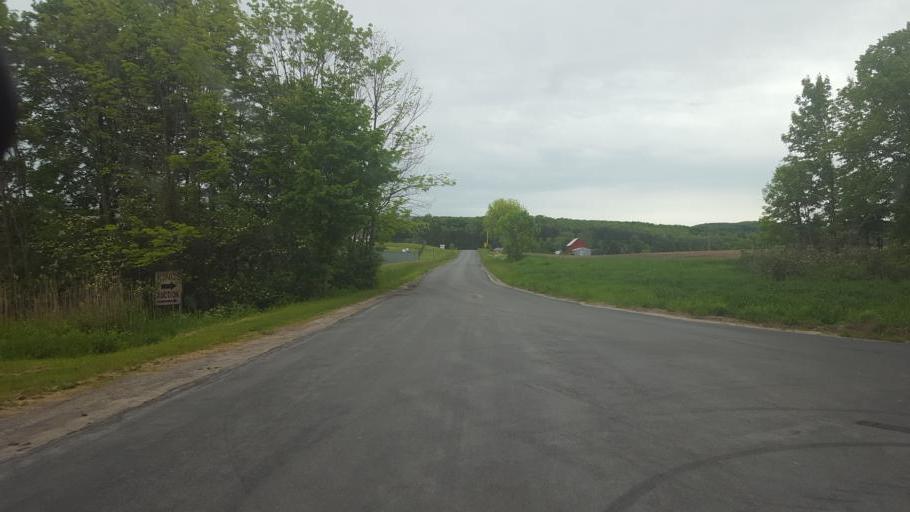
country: US
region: New York
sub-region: Oneida County
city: Chadwicks
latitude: 42.8764
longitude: -75.1709
